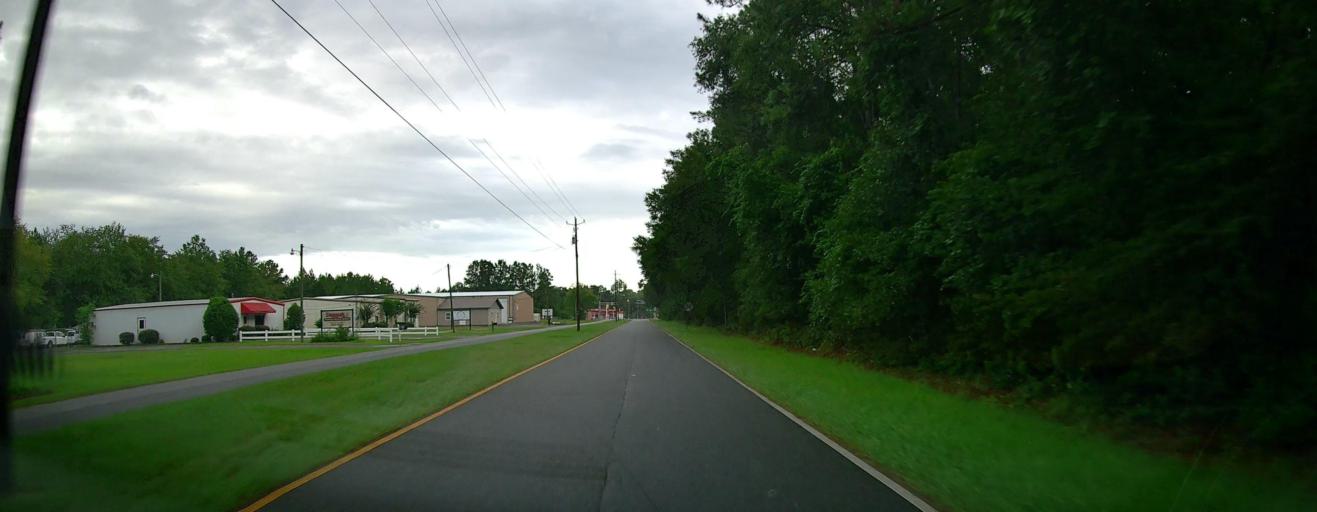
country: US
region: Georgia
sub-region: Ware County
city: Deenwood
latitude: 31.2201
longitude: -82.3880
